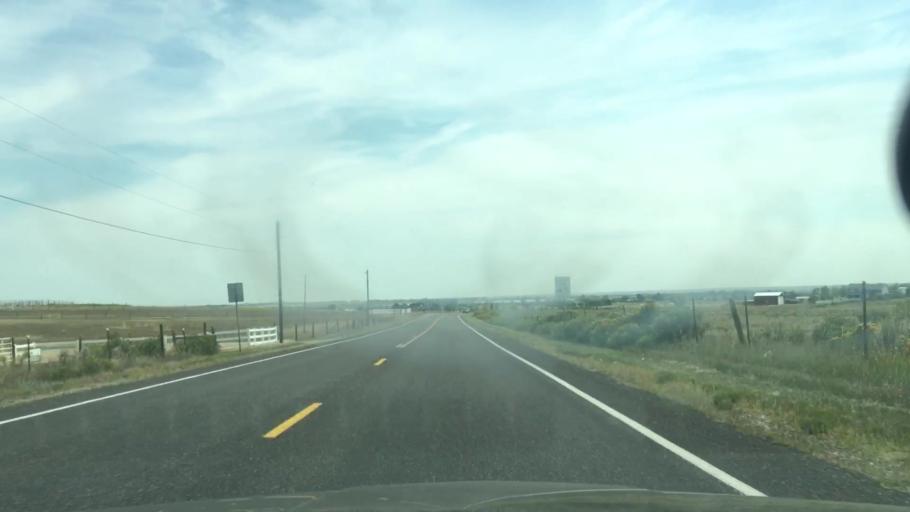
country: US
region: Colorado
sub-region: Larimer County
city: Campion
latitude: 40.3367
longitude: -105.1736
